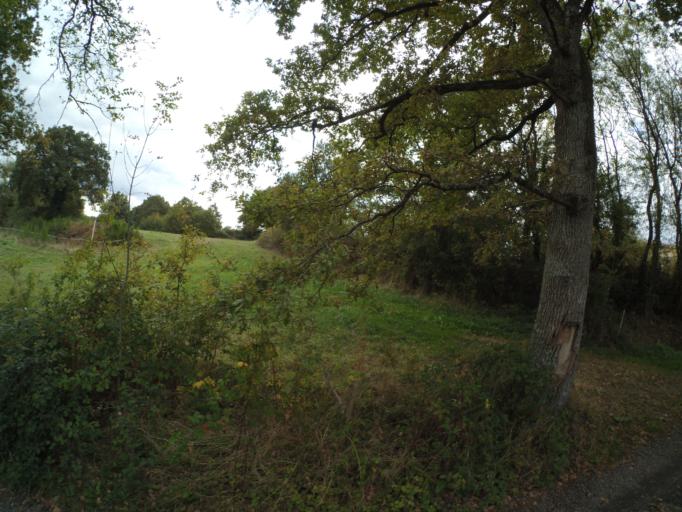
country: FR
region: Pays de la Loire
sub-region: Departement de la Loire-Atlantique
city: Remouille
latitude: 47.0714
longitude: -1.3744
